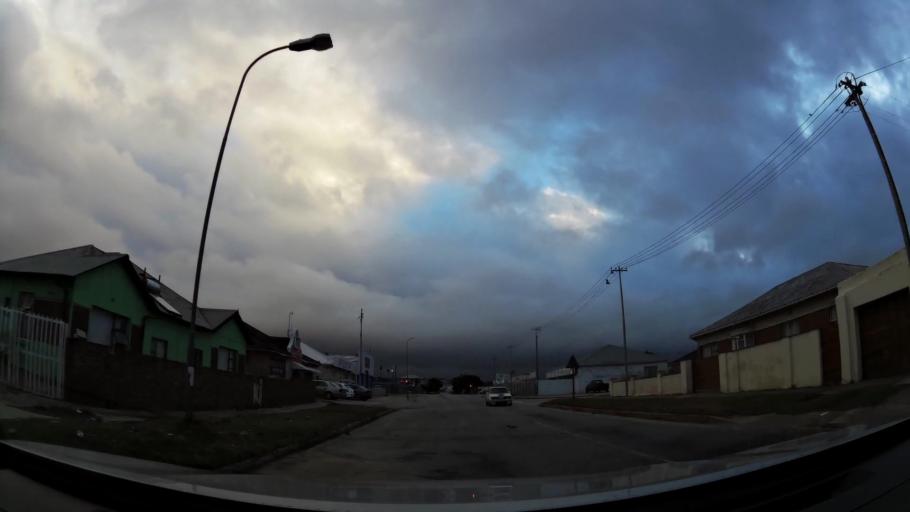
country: ZA
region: Eastern Cape
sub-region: Nelson Mandela Bay Metropolitan Municipality
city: Port Elizabeth
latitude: -33.9265
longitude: 25.5999
